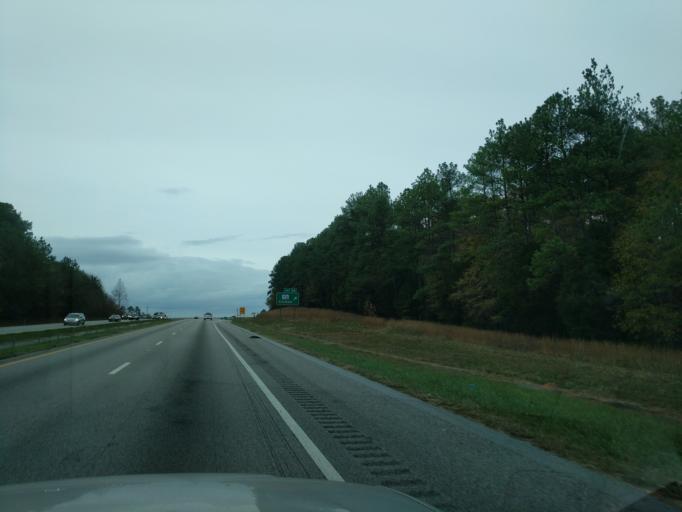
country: US
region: South Carolina
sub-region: Laurens County
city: Clinton
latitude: 34.4932
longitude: -81.8400
